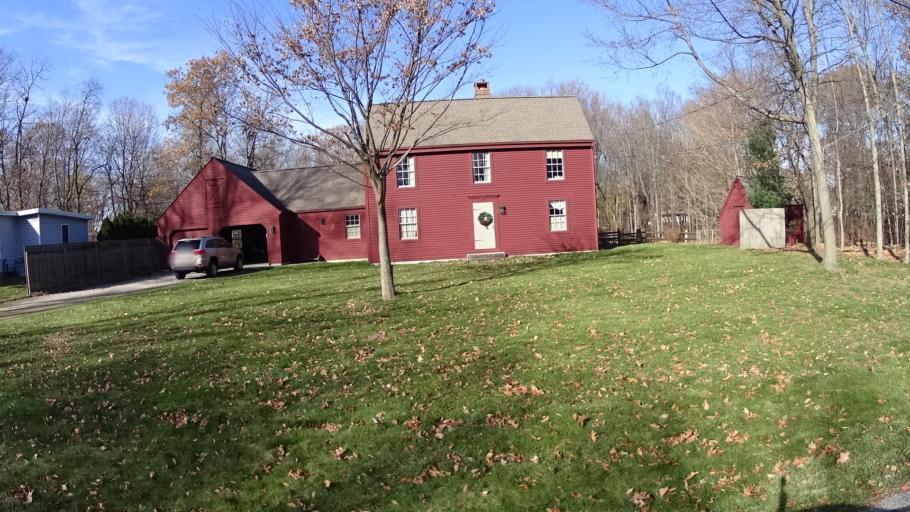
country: US
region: Ohio
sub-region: Lorain County
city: Avon
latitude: 41.4479
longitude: -82.0362
